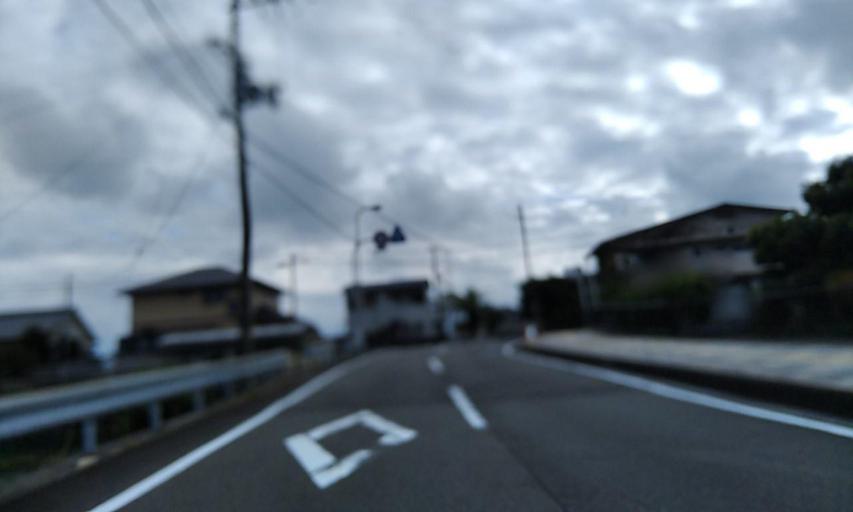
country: JP
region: Wakayama
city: Shingu
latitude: 33.5896
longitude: 135.9529
